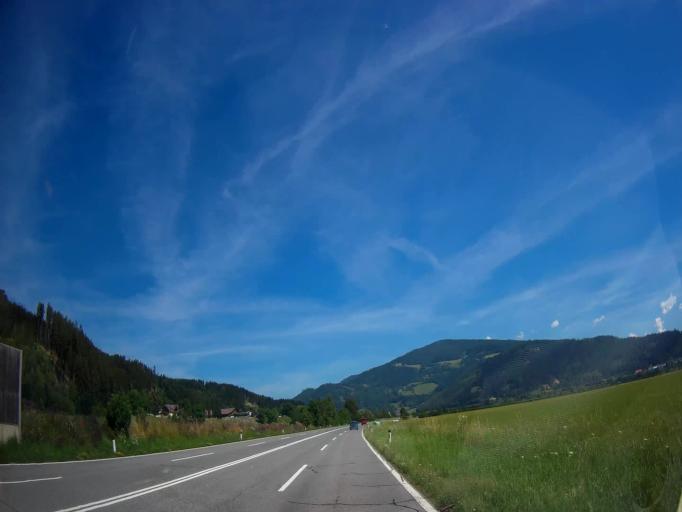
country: AT
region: Carinthia
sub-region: Politischer Bezirk Sankt Veit an der Glan
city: Molbling
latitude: 46.8671
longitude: 14.4490
